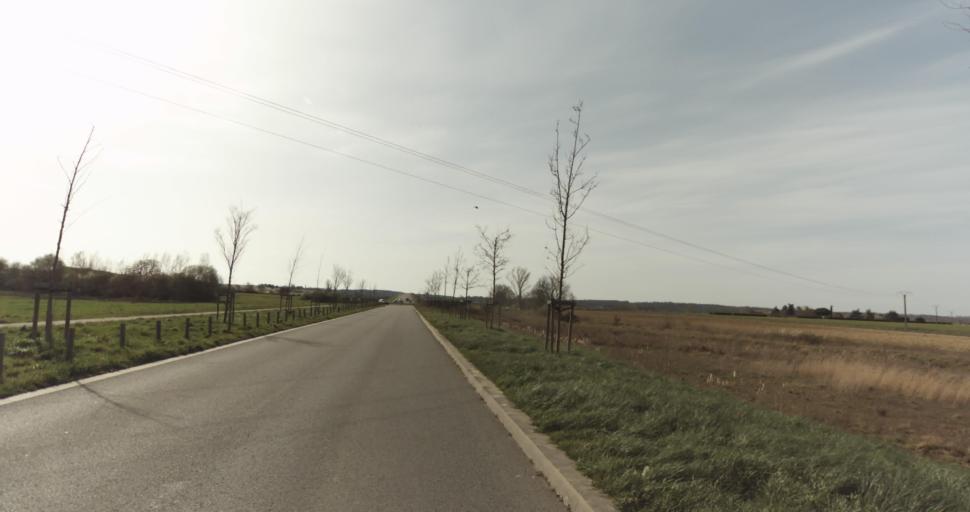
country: FR
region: Midi-Pyrenees
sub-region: Departement de la Haute-Garonne
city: Buzet-sur-Tarn
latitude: 43.7699
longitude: 1.6558
